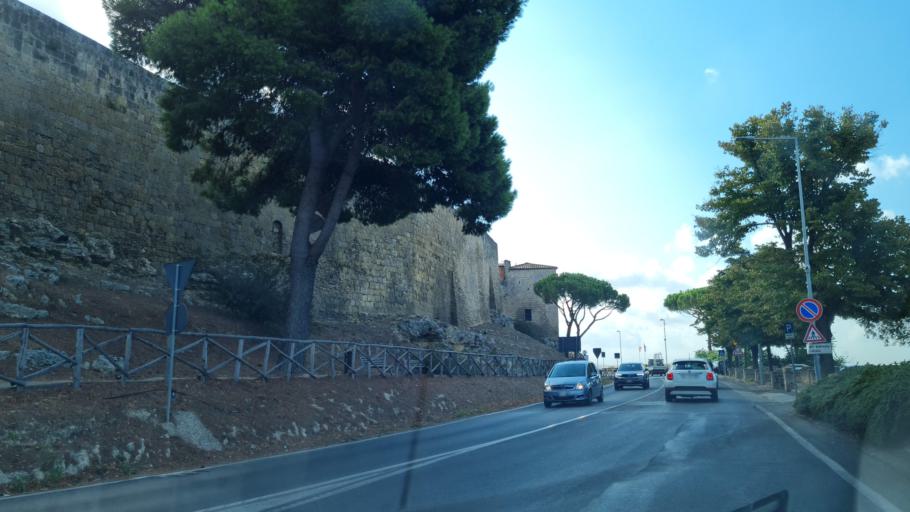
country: IT
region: Latium
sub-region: Provincia di Viterbo
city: Tarquinia
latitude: 42.2523
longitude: 11.7529
